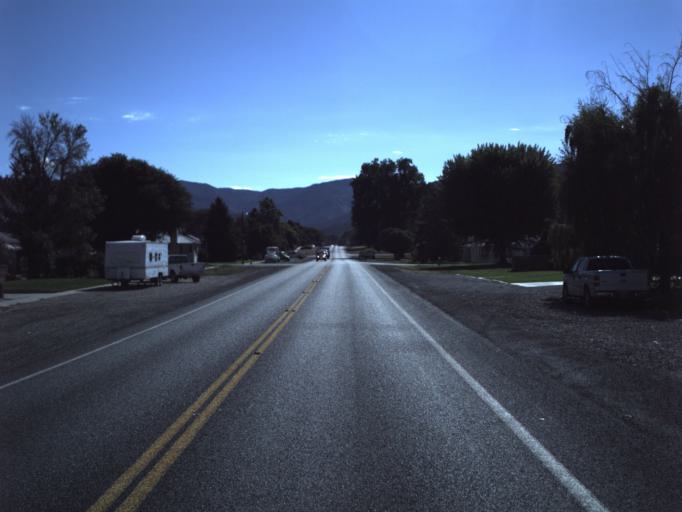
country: US
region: Utah
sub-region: Beaver County
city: Beaver
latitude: 38.2769
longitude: -112.6375
